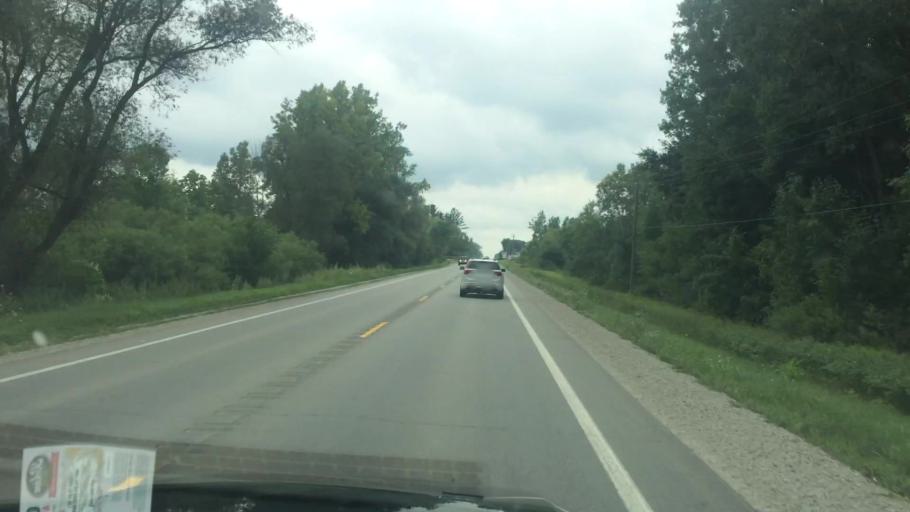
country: US
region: Michigan
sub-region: Tuscola County
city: Cass City
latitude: 43.5940
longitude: -83.0966
